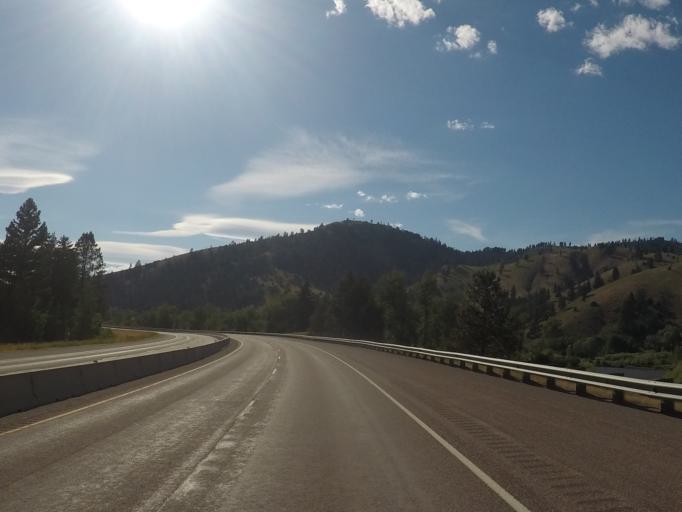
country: US
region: Montana
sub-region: Granite County
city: Philipsburg
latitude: 46.7182
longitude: -113.2927
